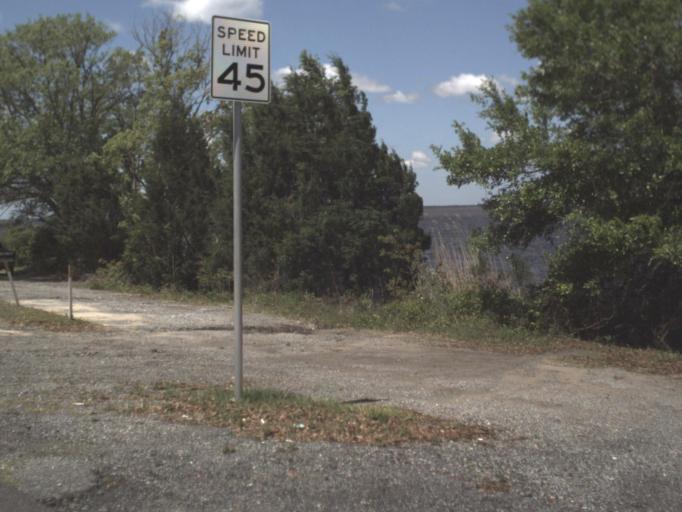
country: US
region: Florida
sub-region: Escambia County
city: Myrtle Grove
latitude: 30.4217
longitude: -87.3486
